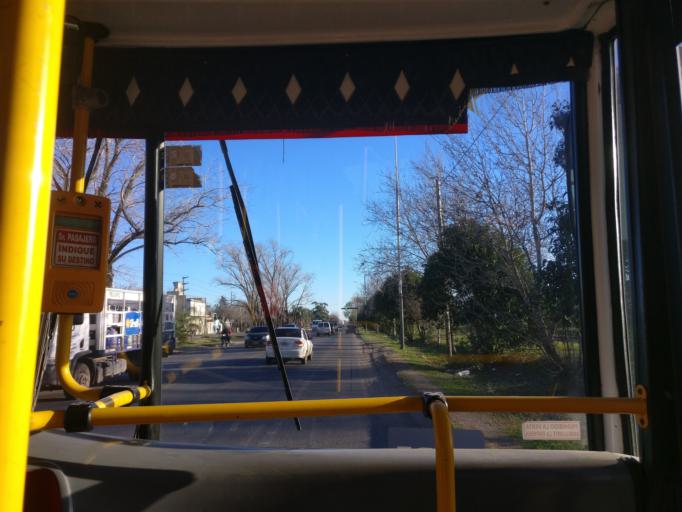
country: AR
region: Buenos Aires
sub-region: Partido de Ezeiza
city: Ezeiza
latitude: -34.9084
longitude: -58.5917
